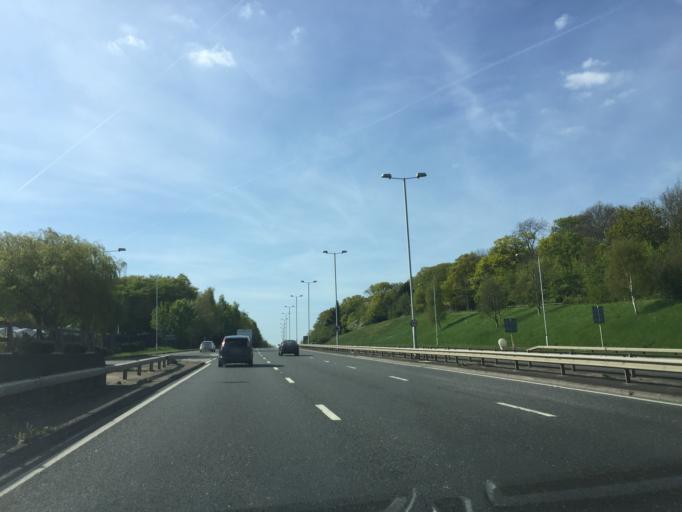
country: GB
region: England
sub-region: Greater London
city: Sidcup
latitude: 51.4199
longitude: 0.0957
